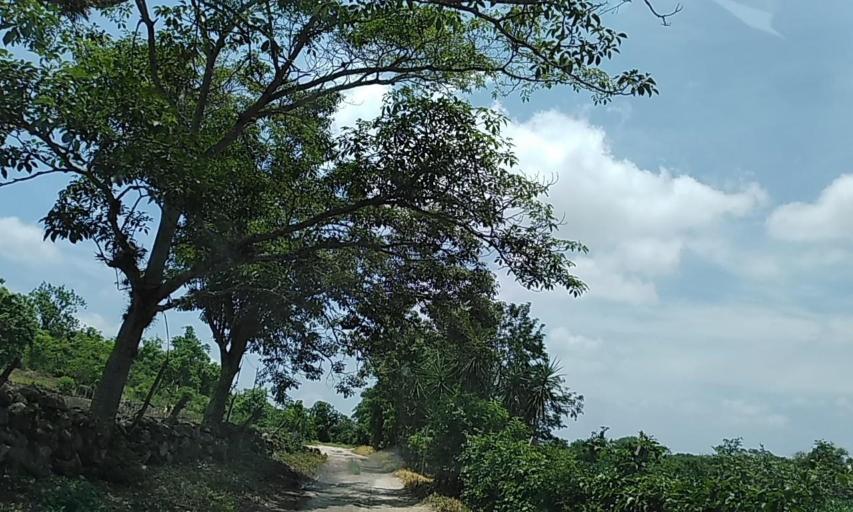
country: MX
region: Veracruz
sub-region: Emiliano Zapata
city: Dos Rios
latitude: 19.4386
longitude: -96.7503
